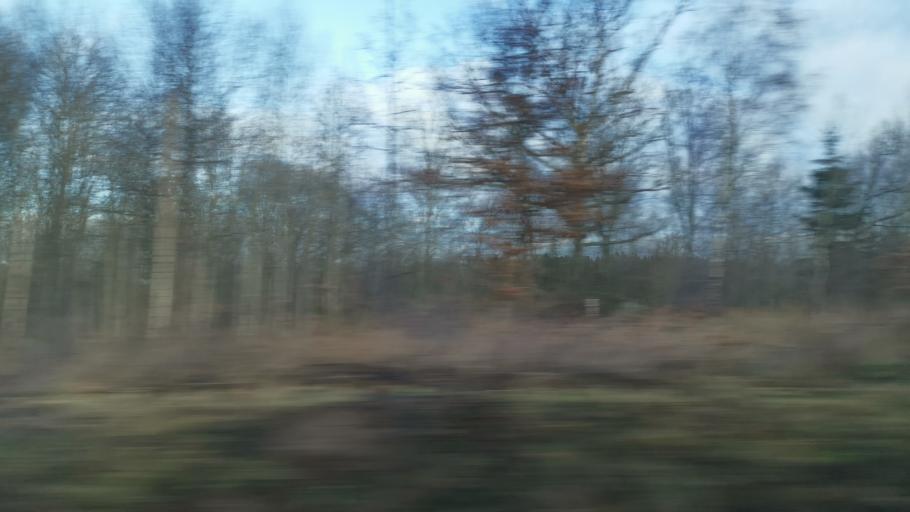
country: SE
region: Soedermanland
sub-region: Katrineholms Kommun
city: Katrineholm
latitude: 58.9995
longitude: 16.1830
